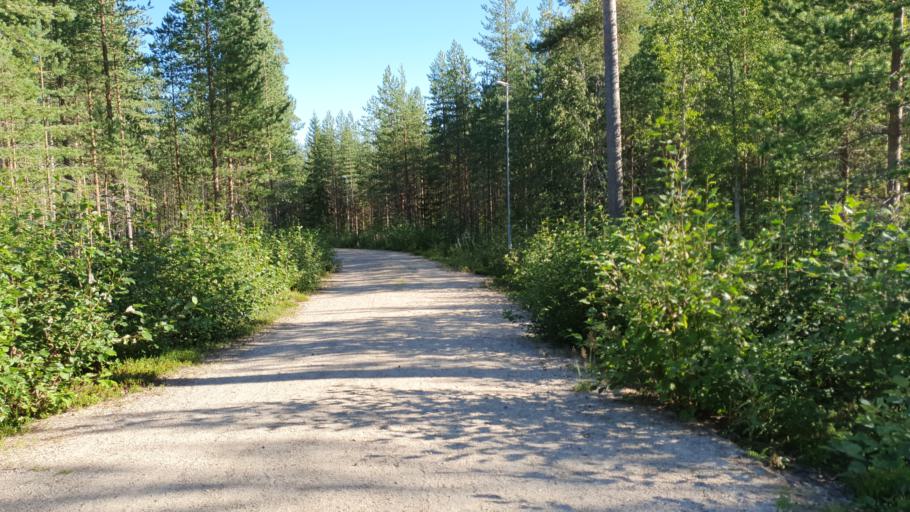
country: FI
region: Kainuu
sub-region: Kehys-Kainuu
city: Kuhmo
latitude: 64.1115
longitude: 29.5103
